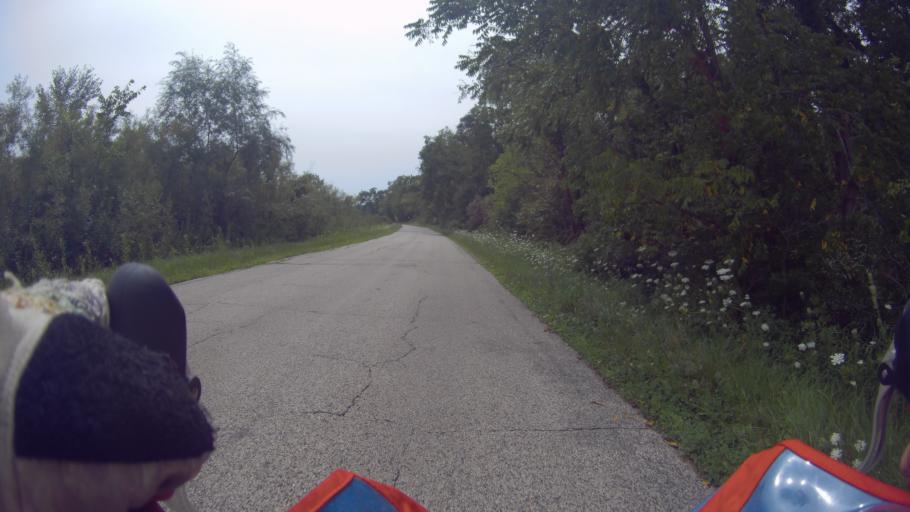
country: US
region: Wisconsin
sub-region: Dane County
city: Mount Horeb
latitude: 42.9665
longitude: -89.6755
